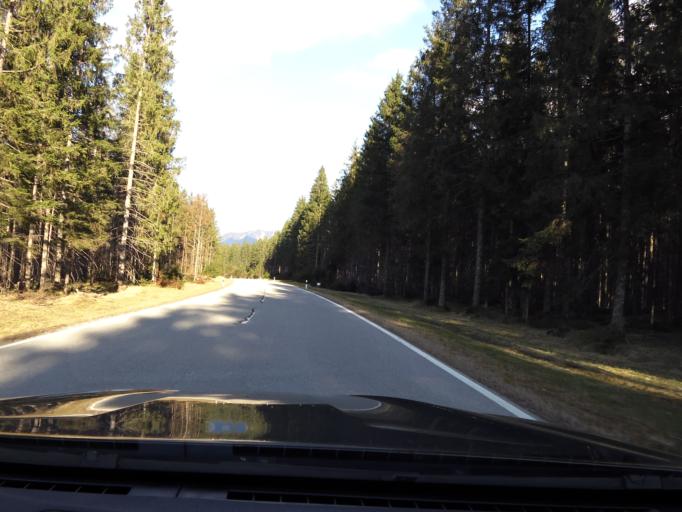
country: DE
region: Bavaria
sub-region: Upper Bavaria
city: Jachenau
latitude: 47.5566
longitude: 11.4481
